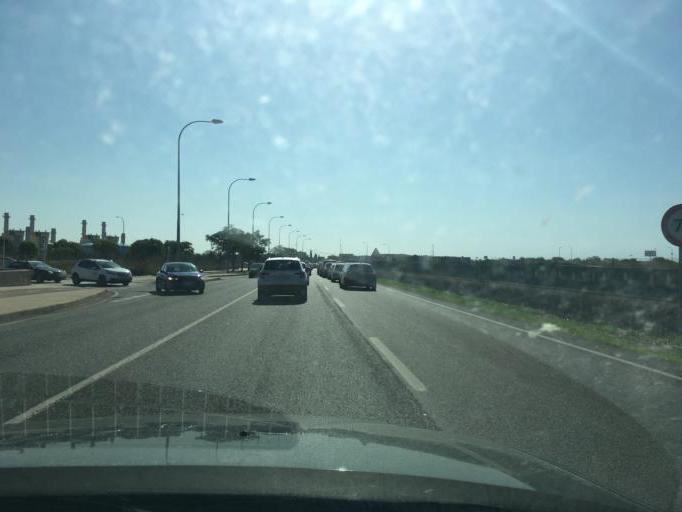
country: ES
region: Balearic Islands
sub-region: Illes Balears
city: Palma
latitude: 39.5732
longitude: 2.6855
